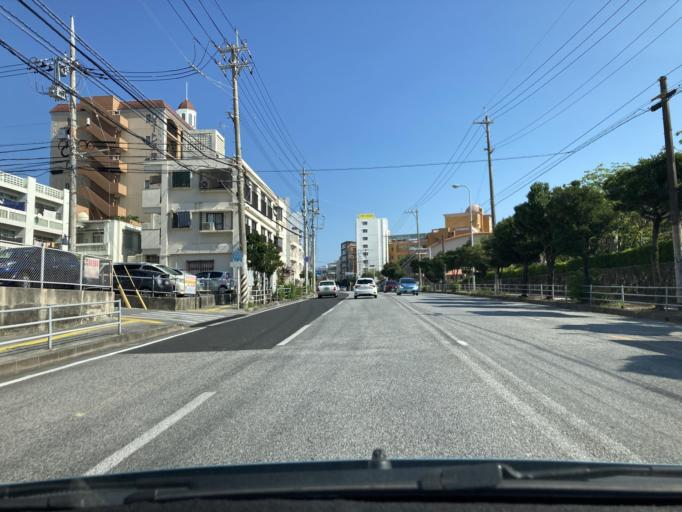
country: JP
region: Okinawa
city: Naha-shi
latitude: 26.2066
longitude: 127.6946
